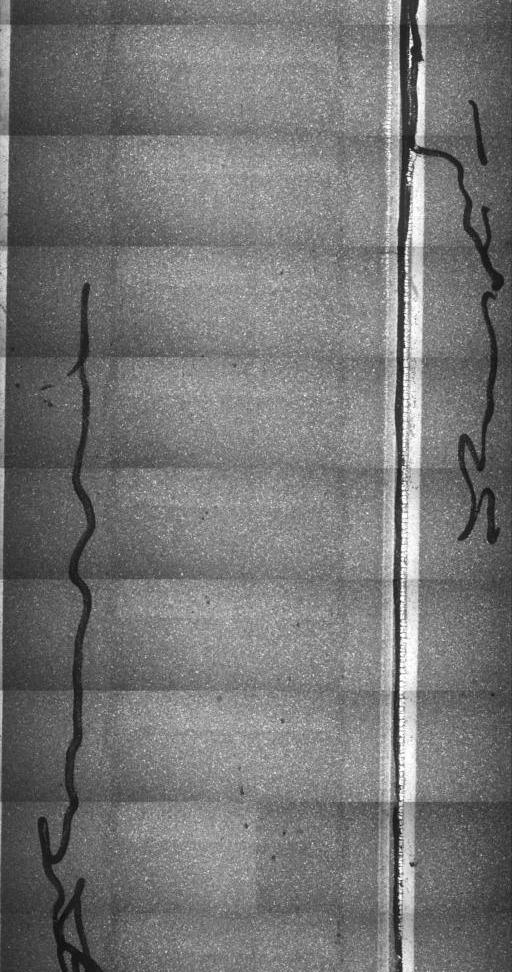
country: CA
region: Quebec
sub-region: Estrie
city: Coaticook
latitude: 45.0045
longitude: -71.7990
